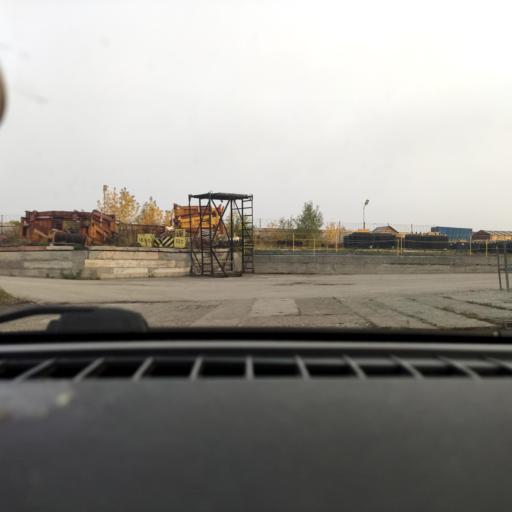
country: RU
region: Perm
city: Kondratovo
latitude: 58.0114
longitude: 56.1623
